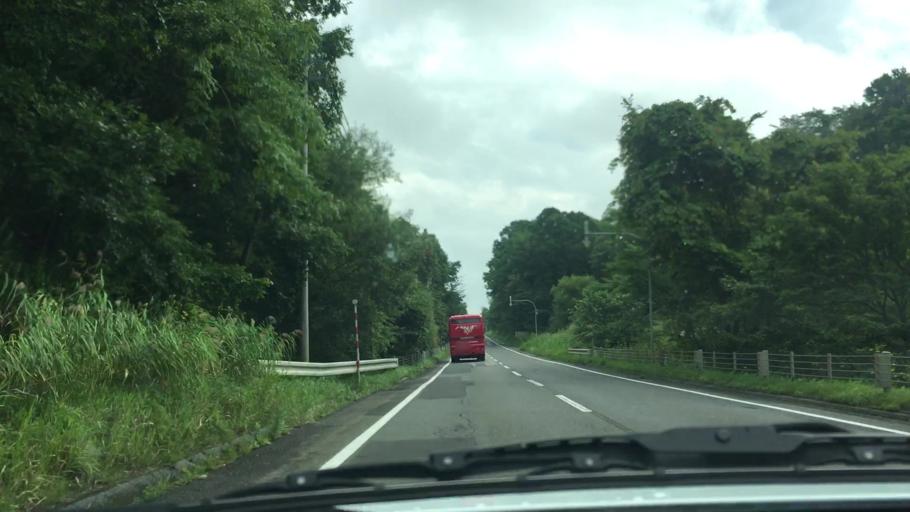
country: JP
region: Hokkaido
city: Chitose
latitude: 42.9432
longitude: 141.7505
